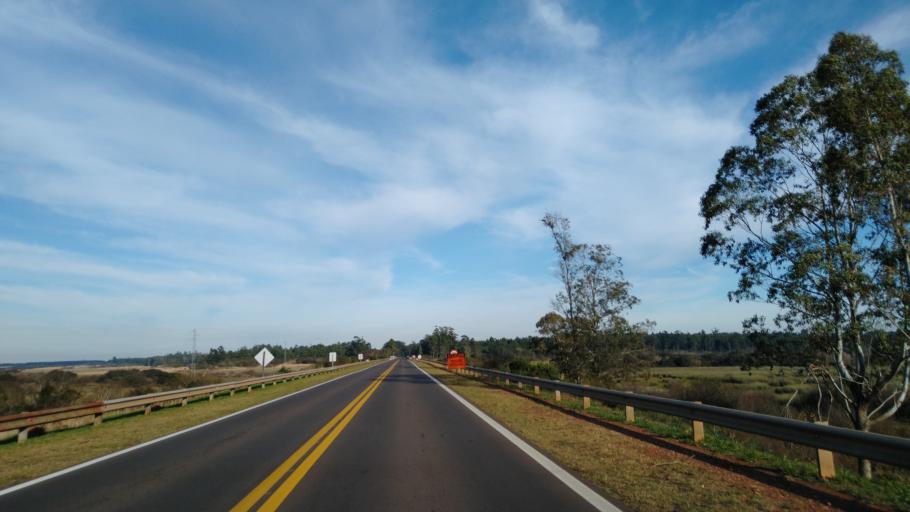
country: AR
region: Corrientes
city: Yapeyu
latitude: -29.4228
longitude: -56.8491
